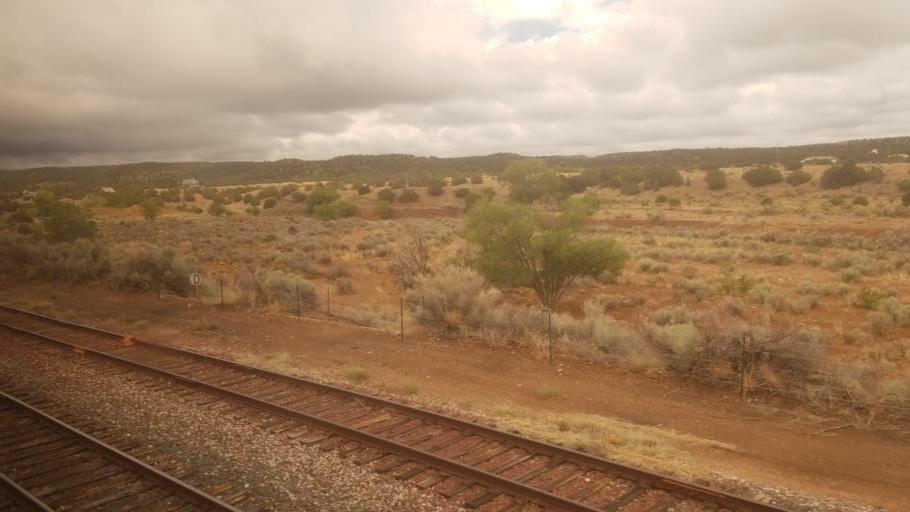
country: US
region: New Mexico
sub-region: Santa Fe County
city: Eldorado at Santa Fe
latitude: 35.4776
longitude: -105.8844
